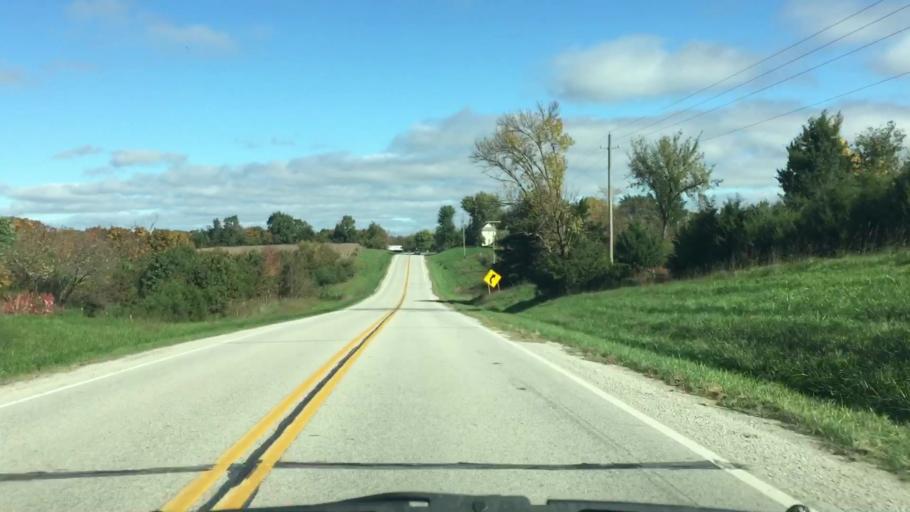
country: US
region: Iowa
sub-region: Decatur County
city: Leon
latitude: 40.6940
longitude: -93.7746
